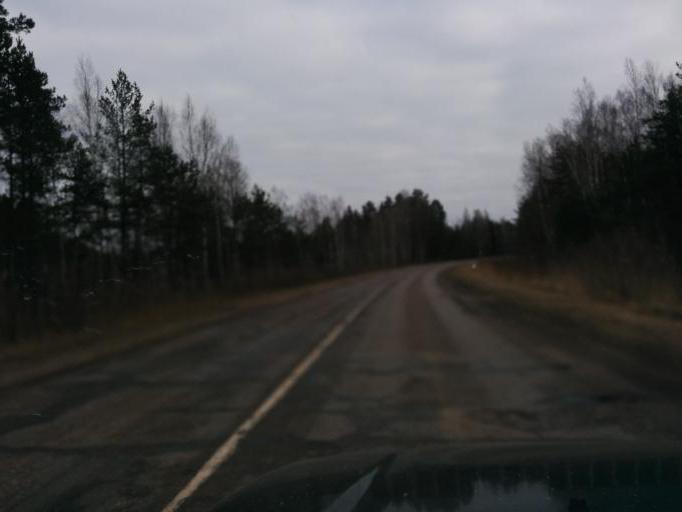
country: LV
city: Tireli
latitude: 56.8595
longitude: 23.5363
